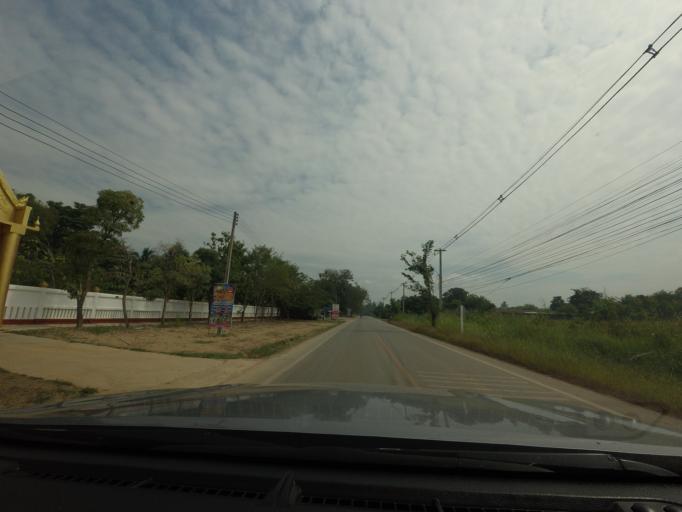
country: TH
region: Phitsanulok
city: Phitsanulok
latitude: 16.7244
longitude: 100.3113
